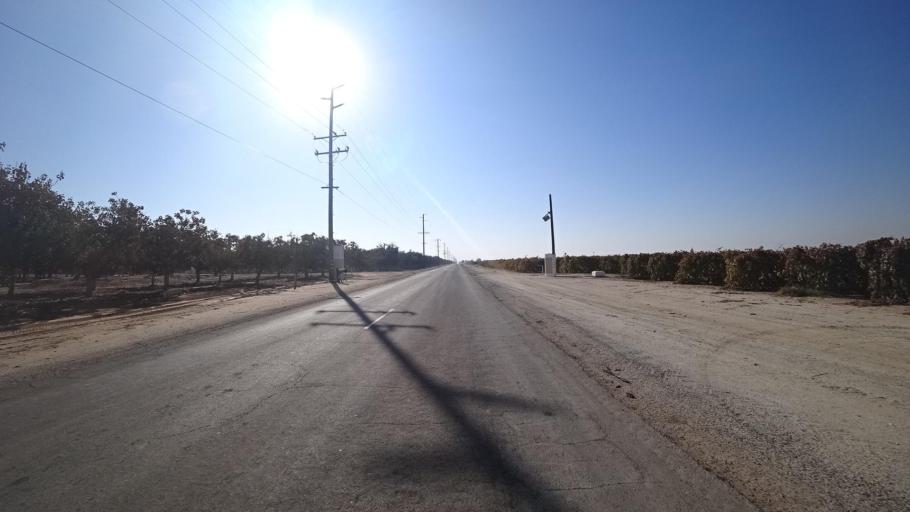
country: US
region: California
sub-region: Kern County
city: McFarland
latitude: 35.7257
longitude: -119.2051
